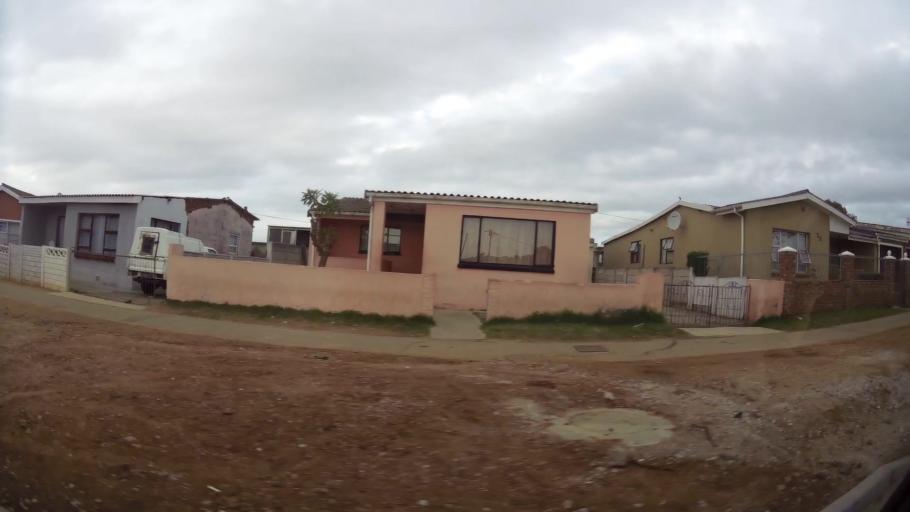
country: ZA
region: Eastern Cape
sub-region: Nelson Mandela Bay Metropolitan Municipality
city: Port Elizabeth
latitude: -33.9109
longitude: 25.5556
